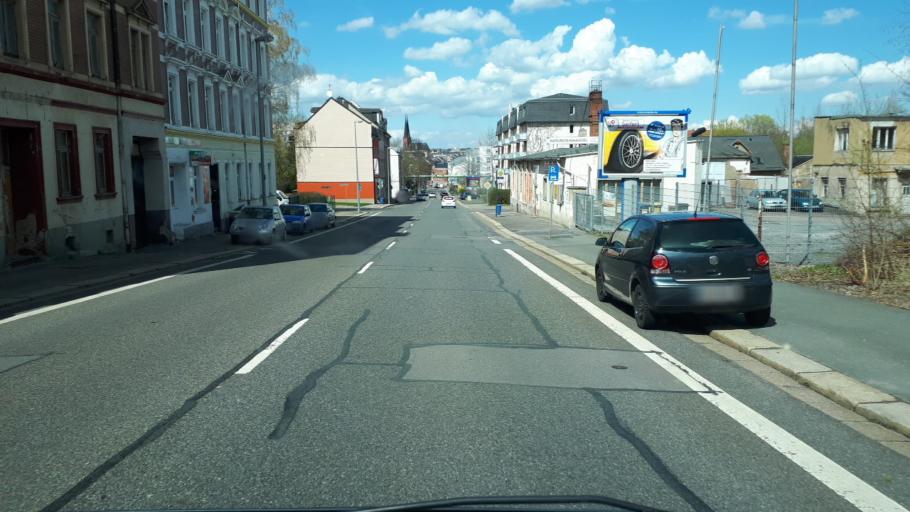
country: DE
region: Saxony
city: Chemnitz
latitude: 50.8251
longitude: 12.9417
